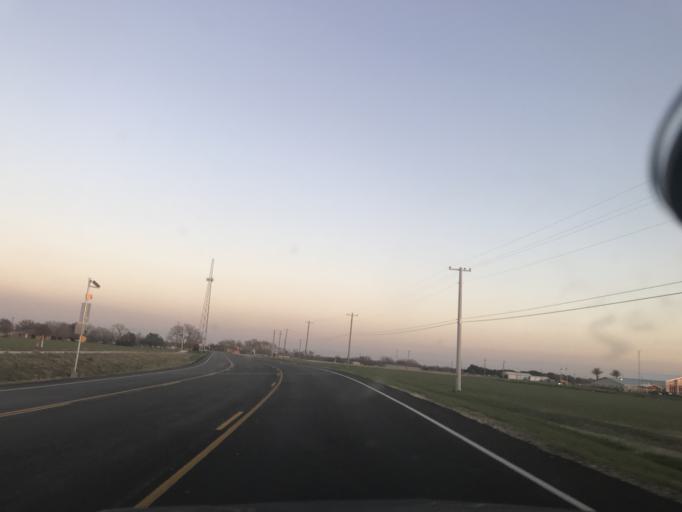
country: US
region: Texas
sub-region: Williamson County
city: Hutto
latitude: 30.5191
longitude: -97.5417
